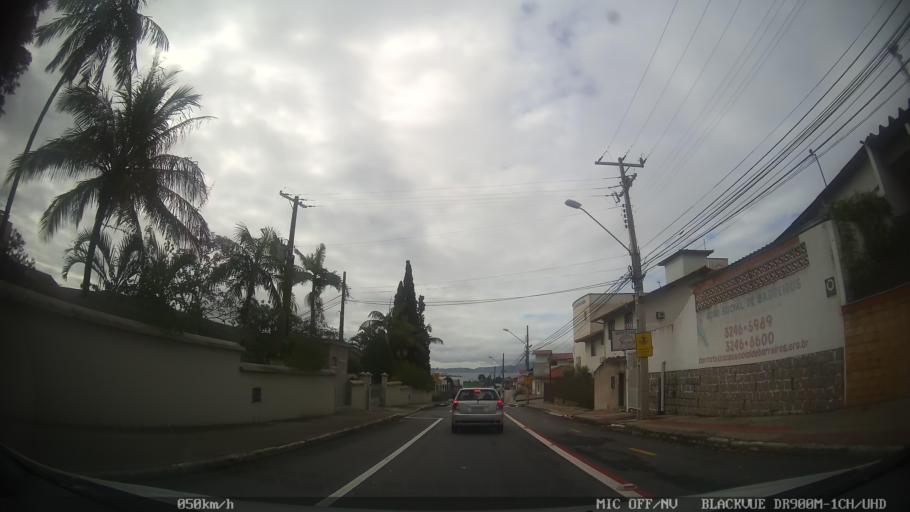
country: BR
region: Santa Catarina
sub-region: Sao Jose
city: Campinas
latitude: -27.5671
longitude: -48.6181
